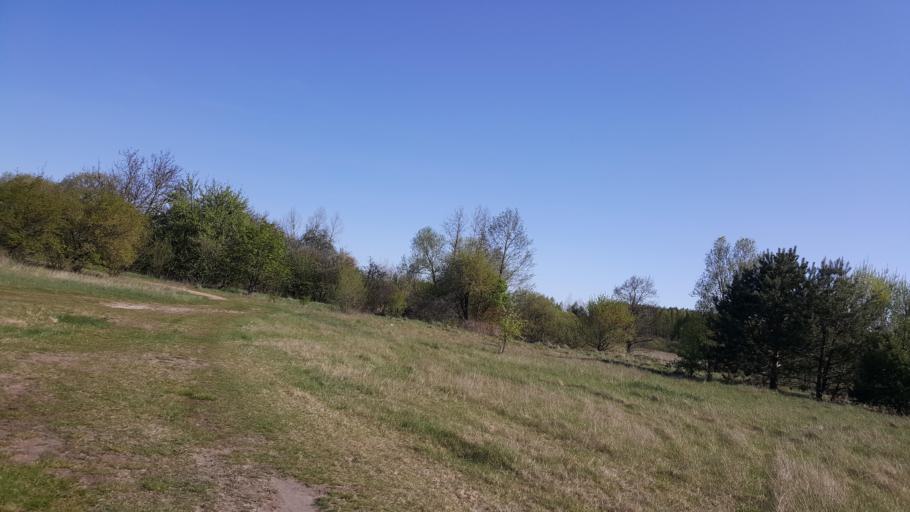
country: BY
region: Brest
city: Kamyanyets
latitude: 52.4415
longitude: 23.8817
